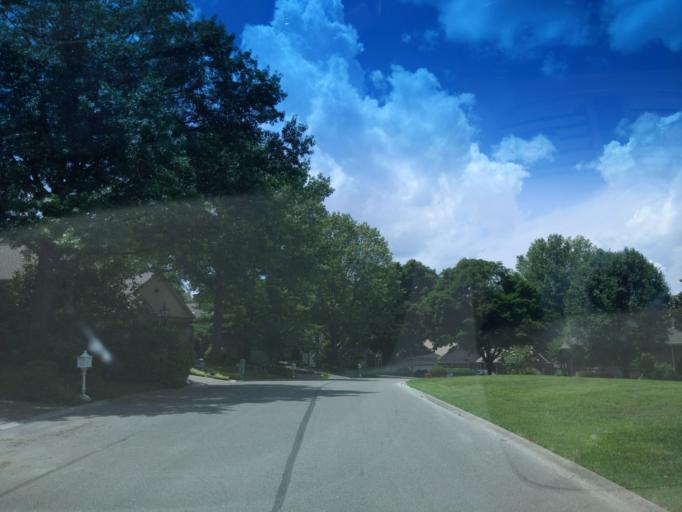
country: US
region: Tennessee
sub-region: Williamson County
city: Brentwood
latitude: 36.0442
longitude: -86.7675
